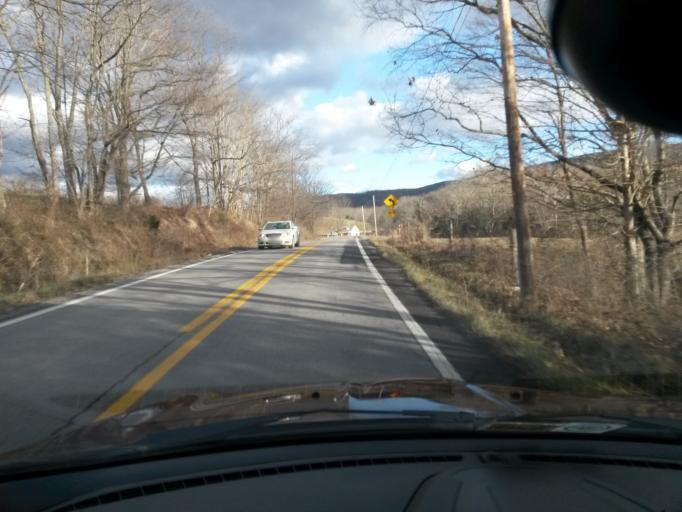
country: US
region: West Virginia
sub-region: Monroe County
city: Union
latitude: 37.4782
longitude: -80.6332
